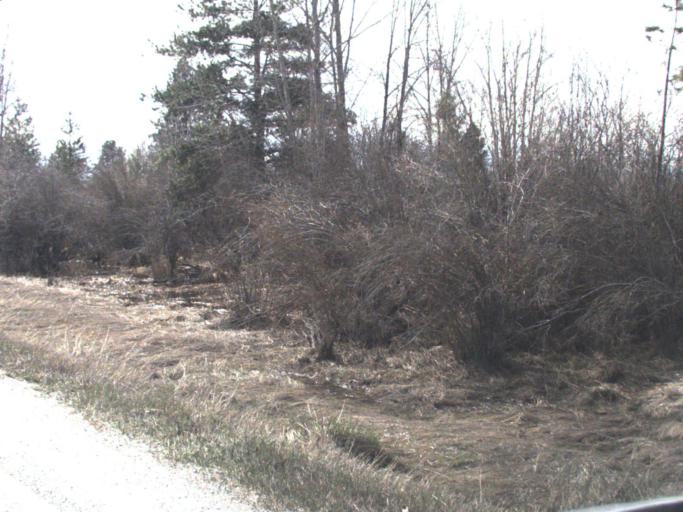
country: US
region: Washington
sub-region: Pend Oreille County
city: Newport
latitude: 48.3827
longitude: -117.3093
